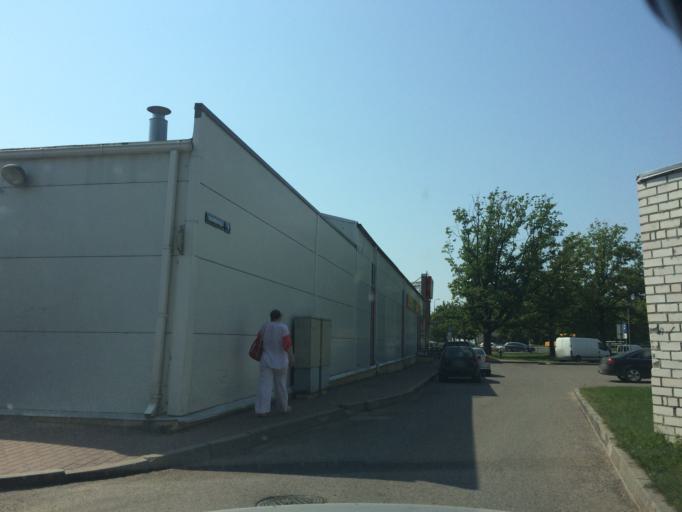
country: LV
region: Rezekne
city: Rezekne
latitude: 56.5023
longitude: 27.3302
